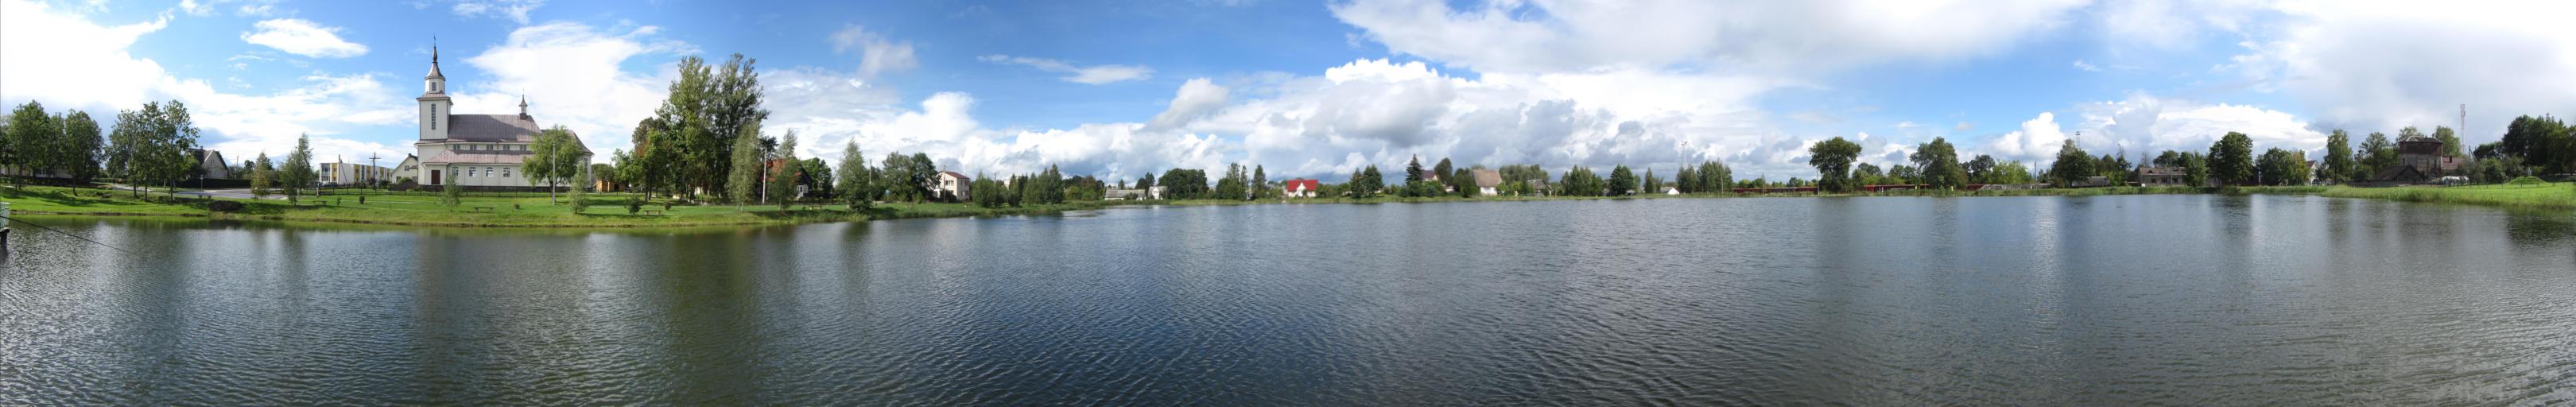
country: LT
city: Dukstas
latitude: 55.5212
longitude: 26.3229
